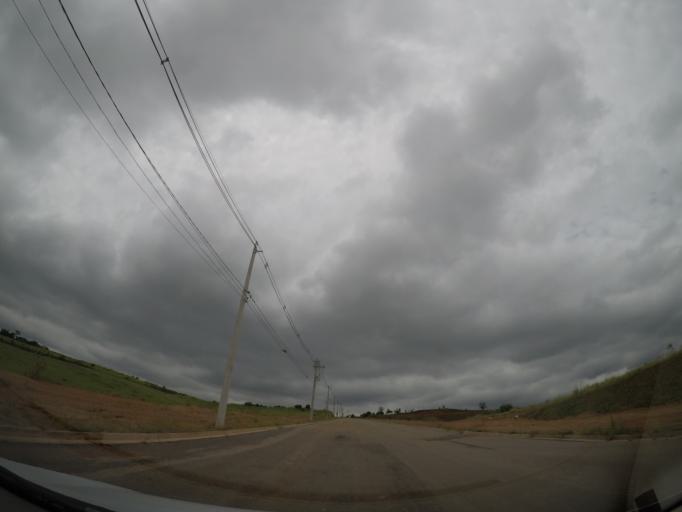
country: BR
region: Sao Paulo
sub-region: Vinhedo
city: Vinhedo
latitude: -23.0759
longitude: -47.0095
